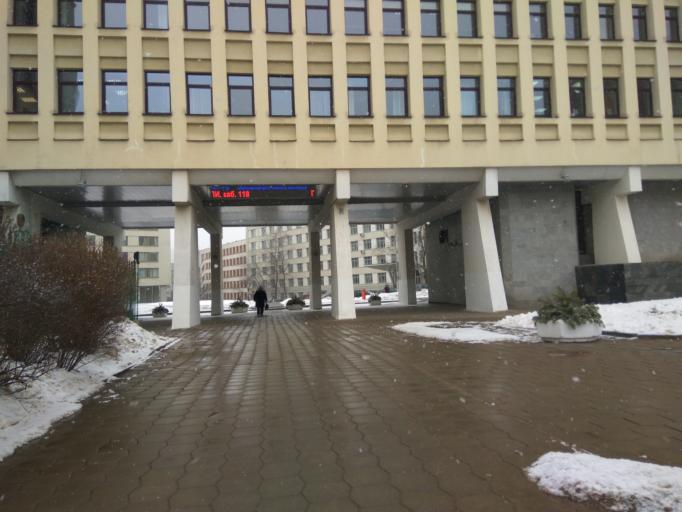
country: BY
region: Minsk
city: Minsk
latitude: 53.8966
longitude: 27.5466
